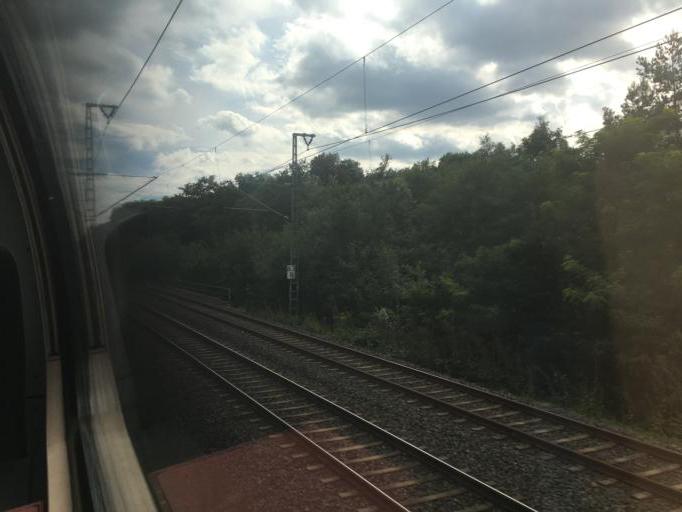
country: DE
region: Hesse
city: Dreieich
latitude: 50.0280
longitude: 8.6621
